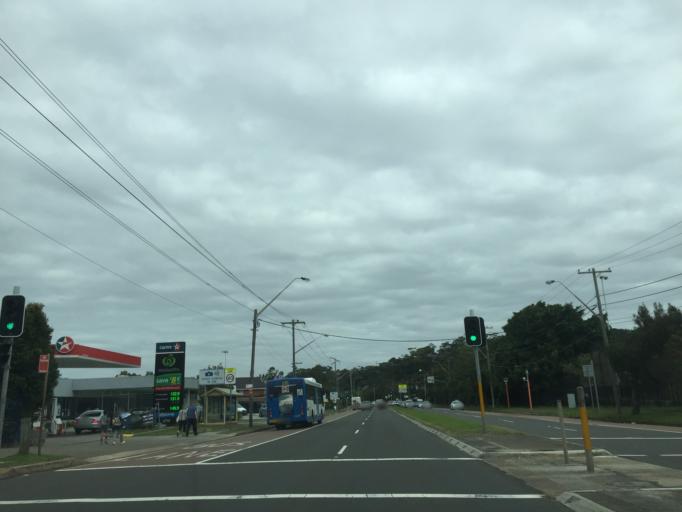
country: AU
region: New South Wales
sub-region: Pittwater
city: North Narrabeen
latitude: -33.7004
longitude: 151.2997
